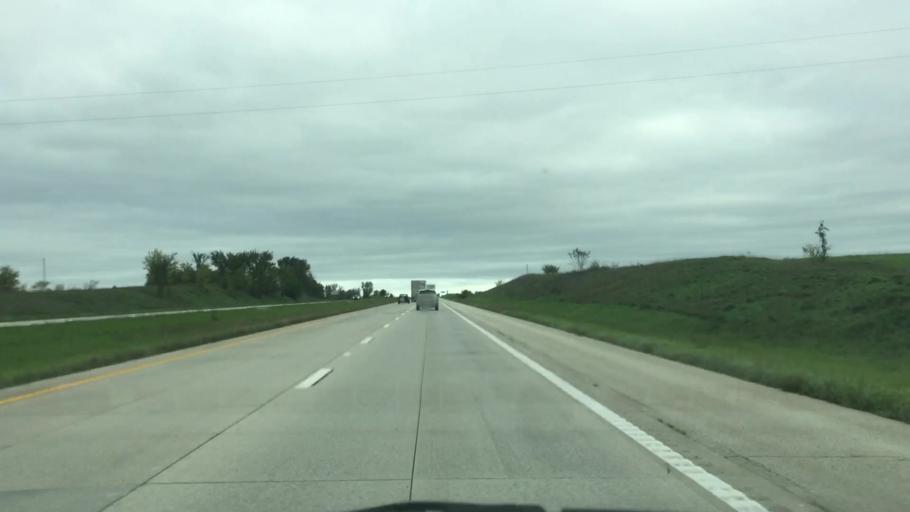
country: US
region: Missouri
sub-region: Daviess County
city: Gallatin
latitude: 40.0617
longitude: -94.0939
